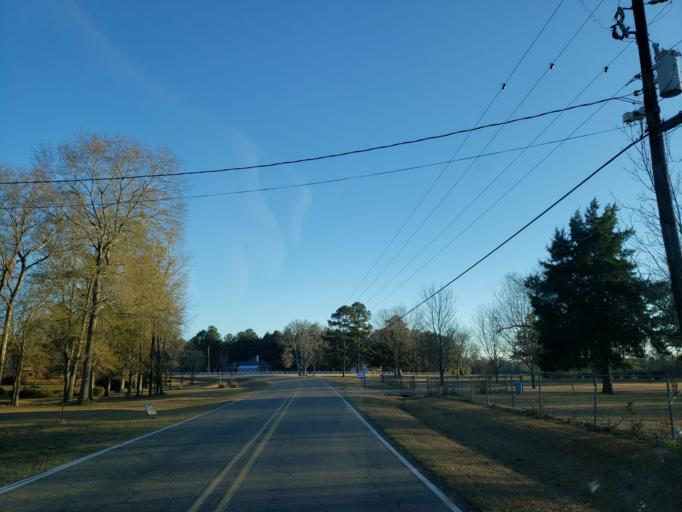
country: US
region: Mississippi
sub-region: Forrest County
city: Rawls Springs
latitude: 31.4350
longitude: -89.3652
